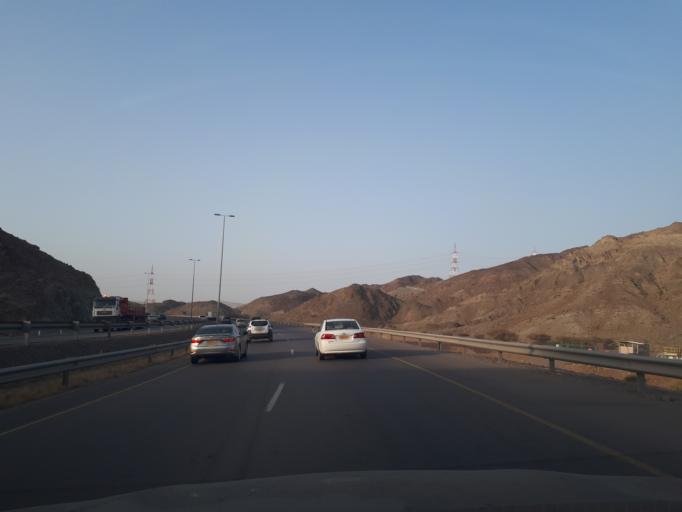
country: OM
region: Muhafazat ad Dakhiliyah
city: Bidbid
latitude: 23.4694
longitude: 58.1952
